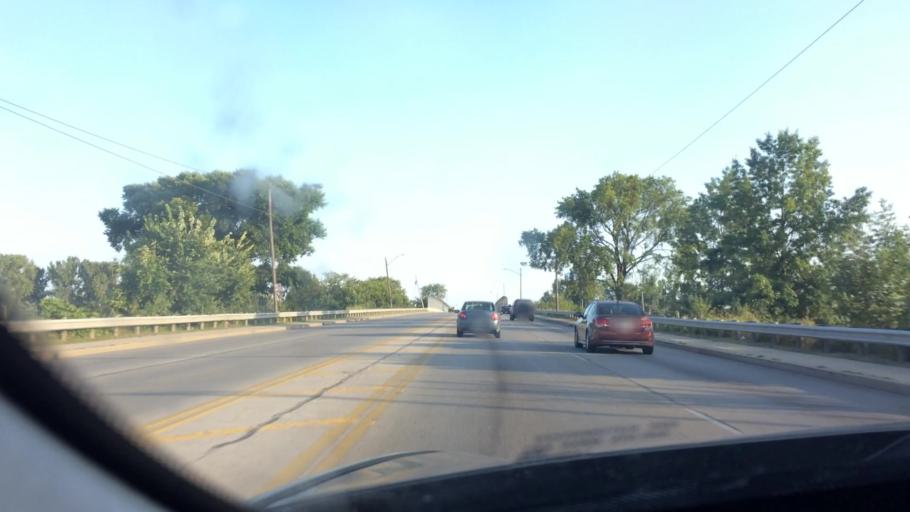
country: US
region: Ohio
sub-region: Lucas County
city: Ottawa Hills
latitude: 41.6339
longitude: -83.6259
